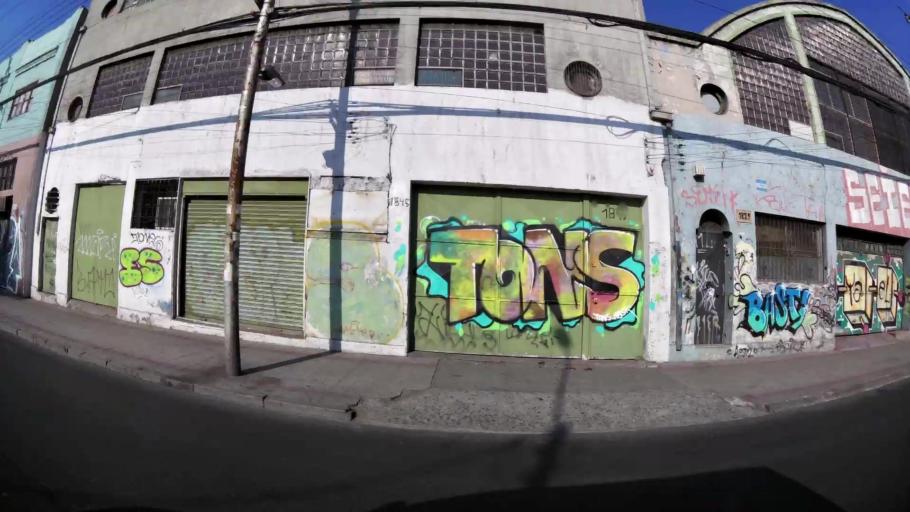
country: CL
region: Santiago Metropolitan
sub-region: Provincia de Santiago
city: Santiago
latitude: -33.4102
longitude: -70.6433
